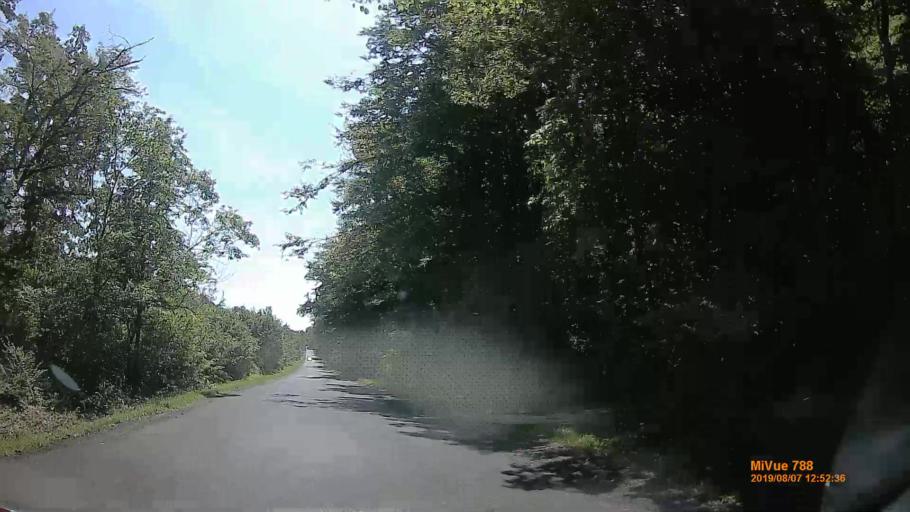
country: HU
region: Zala
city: Cserszegtomaj
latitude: 46.8462
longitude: 17.2672
